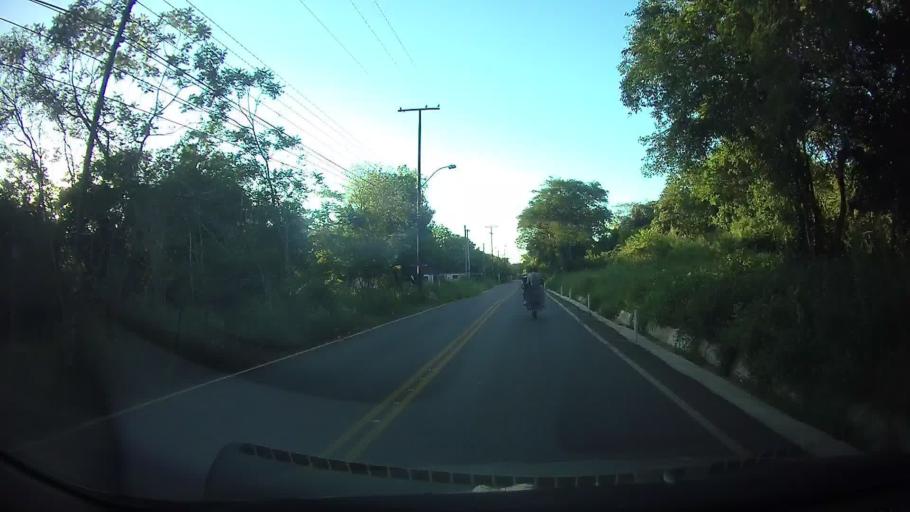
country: PY
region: Central
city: Aregua
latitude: -25.2639
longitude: -57.4358
